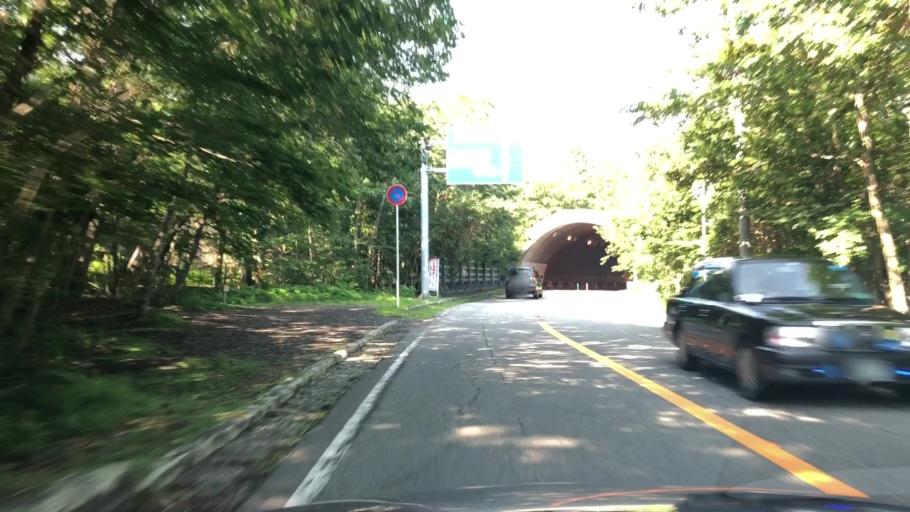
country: JP
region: Shizuoka
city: Gotemba
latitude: 35.3295
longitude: 138.8017
